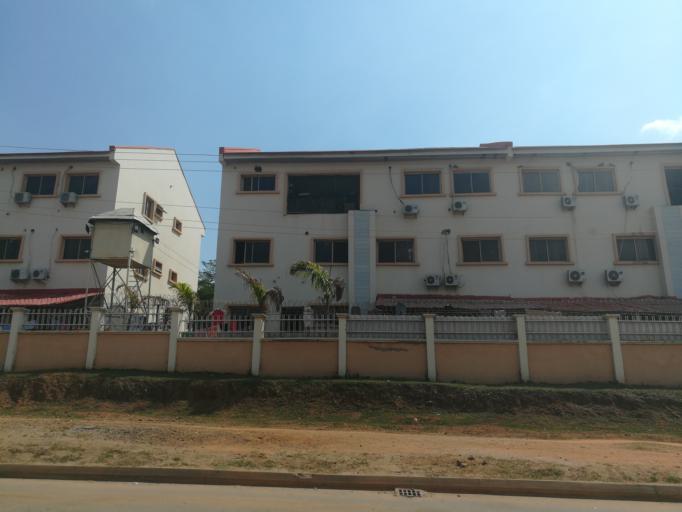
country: NG
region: Abuja Federal Capital Territory
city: Abuja
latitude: 9.0536
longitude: 7.4522
